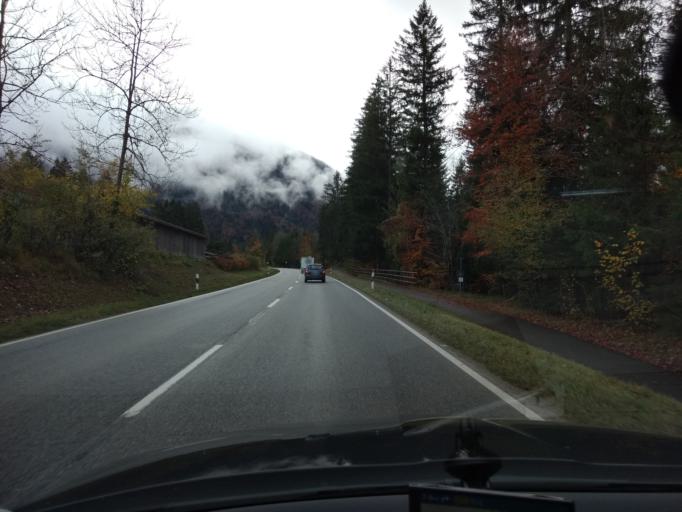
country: DE
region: Bavaria
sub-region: Upper Bavaria
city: Lenggries
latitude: 47.6304
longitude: 11.5941
